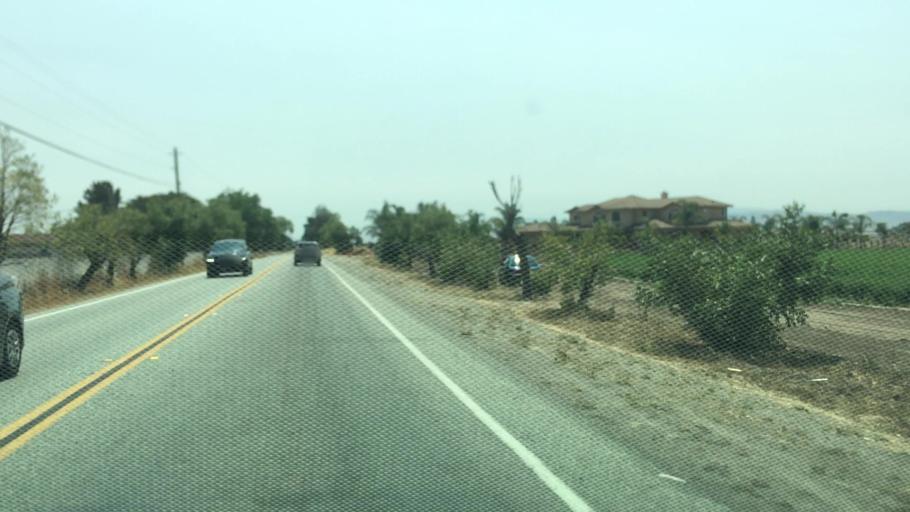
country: US
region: California
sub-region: Santa Clara County
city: Gilroy
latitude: 37.0161
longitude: -121.5196
